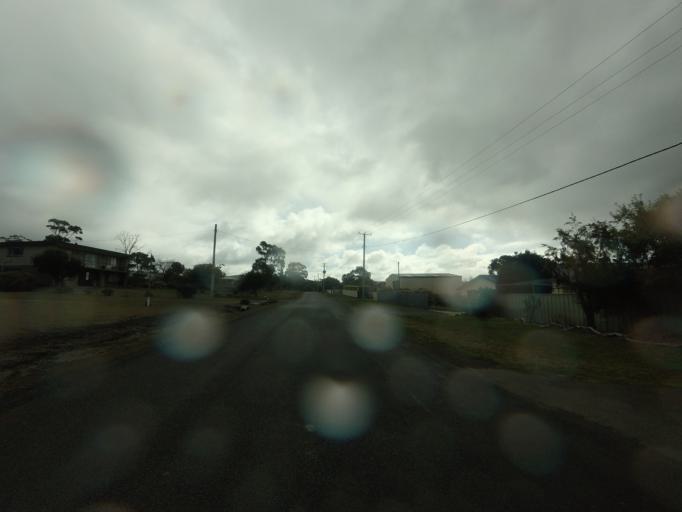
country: AU
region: Tasmania
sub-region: Sorell
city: Sorell
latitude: -42.5271
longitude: 147.9015
